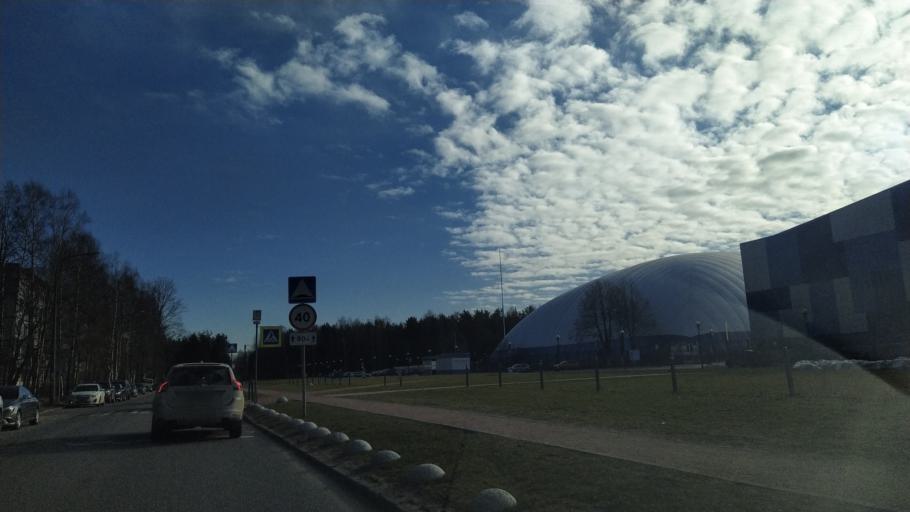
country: RU
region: Leningrad
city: Akademicheskoe
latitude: 60.0047
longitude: 30.4113
